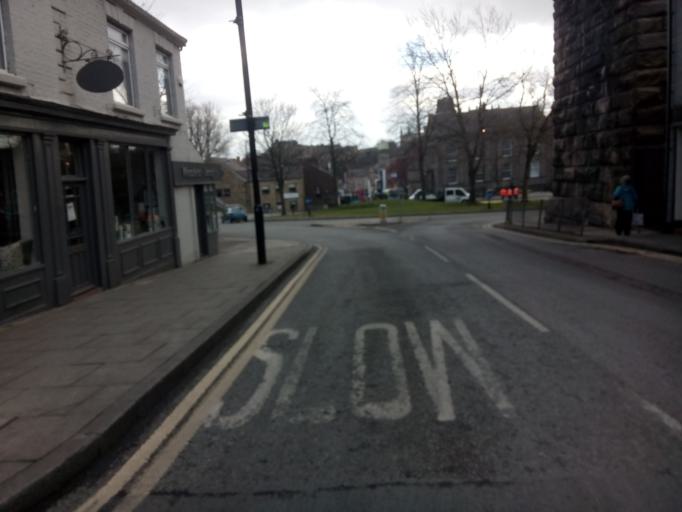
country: GB
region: England
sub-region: County Durham
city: Durham
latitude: 54.7783
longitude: -1.5835
